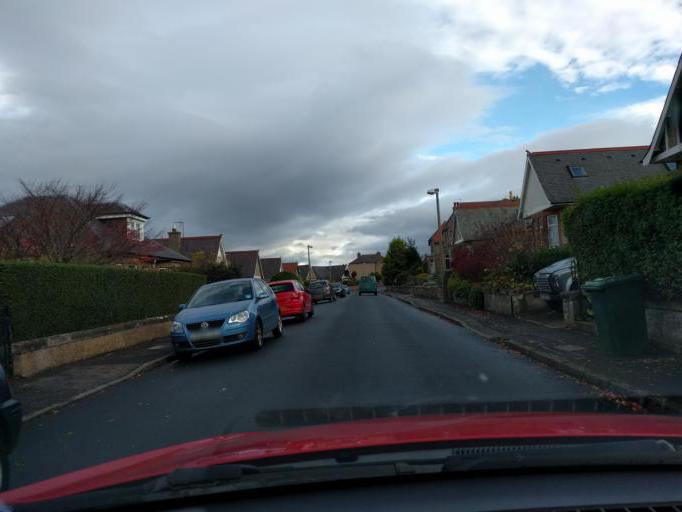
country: GB
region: Scotland
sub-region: Edinburgh
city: Colinton
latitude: 55.9187
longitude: -3.2181
